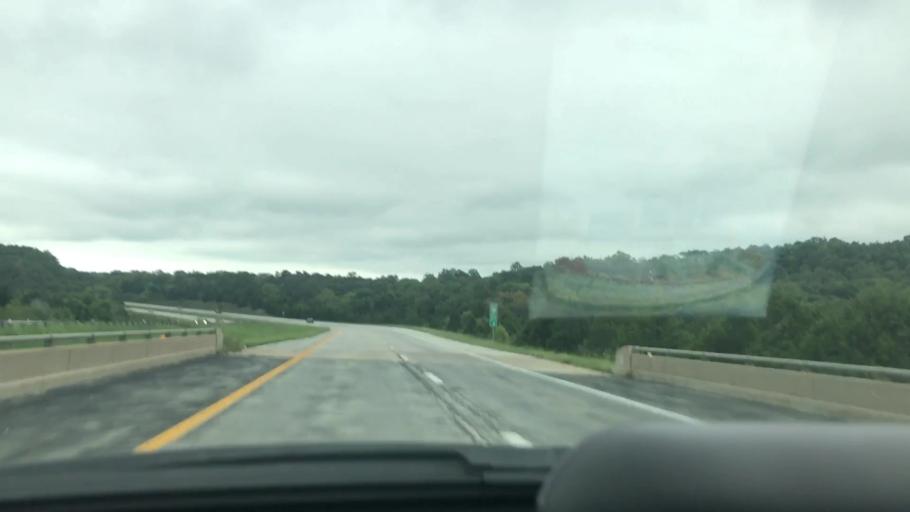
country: US
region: Missouri
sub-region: Greene County
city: Strafford
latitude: 37.2884
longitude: -93.1862
